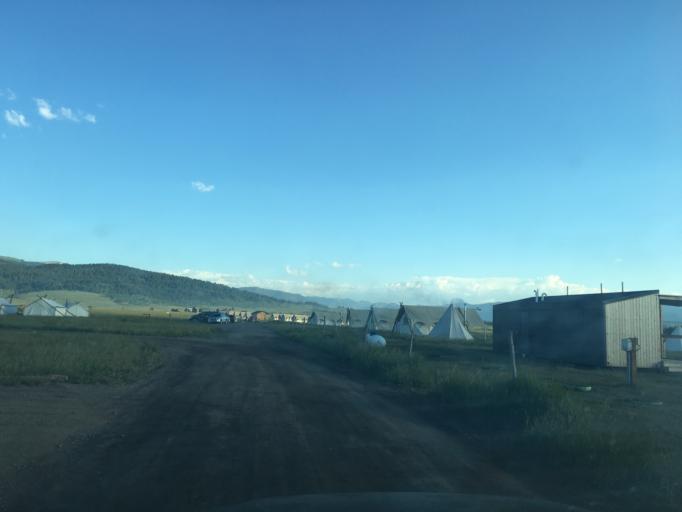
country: US
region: Montana
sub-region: Gallatin County
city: West Yellowstone
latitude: 44.7049
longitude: -111.2112
